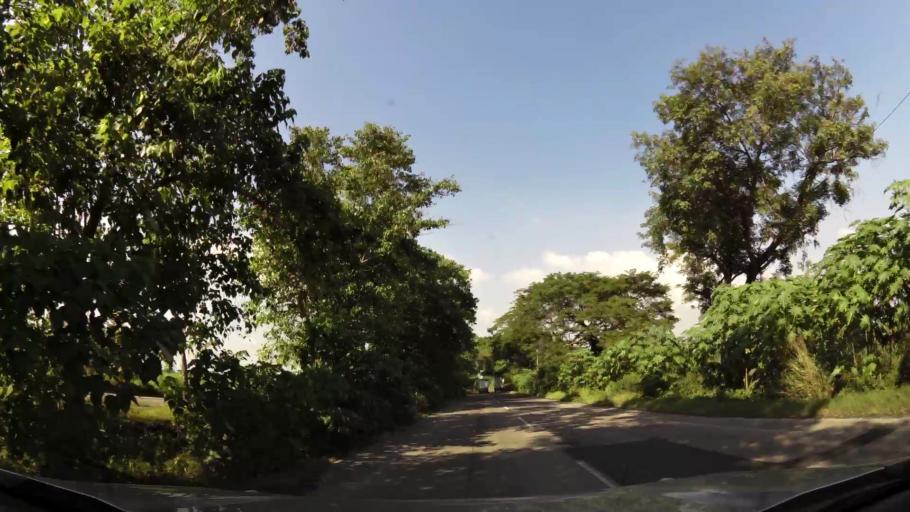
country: GT
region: Escuintla
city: Puerto San Jose
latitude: 13.9904
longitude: -90.7883
